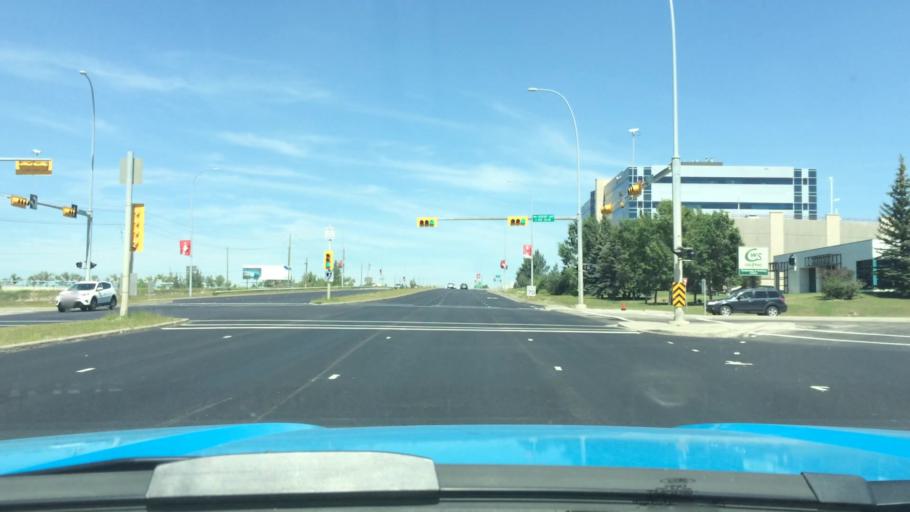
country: CA
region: Alberta
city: Calgary
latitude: 51.0471
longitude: -114.0015
